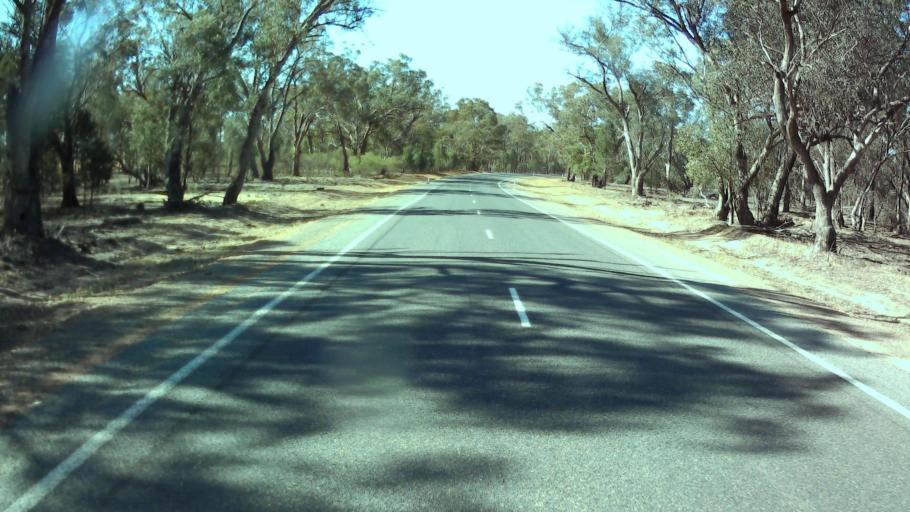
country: AU
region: New South Wales
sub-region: Weddin
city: Grenfell
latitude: -33.7568
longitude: 148.0826
